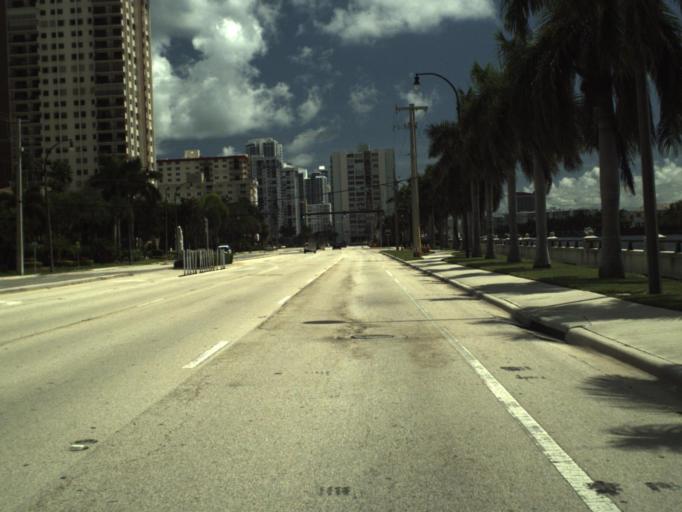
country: US
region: Florida
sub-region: Broward County
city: Hollywood
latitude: 26.0072
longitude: -80.1183
